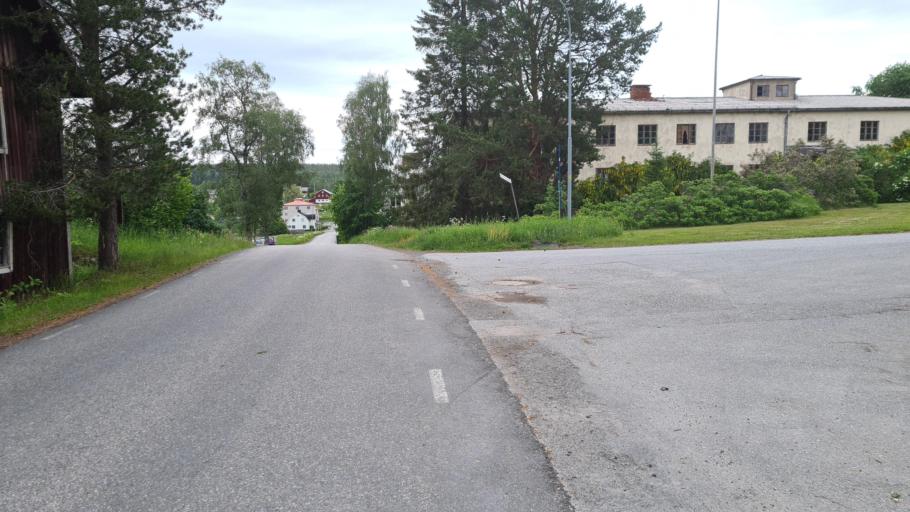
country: SE
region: Vaesternorrland
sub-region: Kramfors Kommun
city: Nordingra
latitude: 62.9834
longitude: 18.4323
